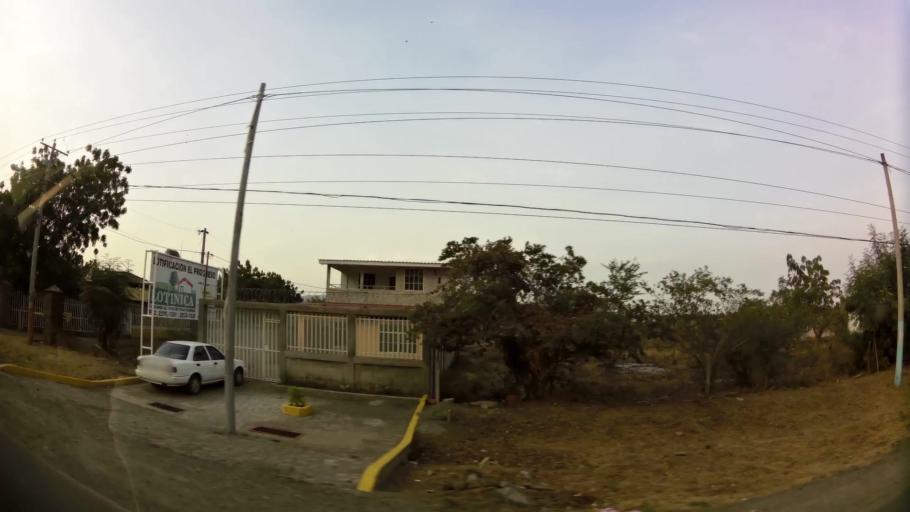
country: NI
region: Managua
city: Ciudad Sandino
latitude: 12.1823
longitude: -86.3578
